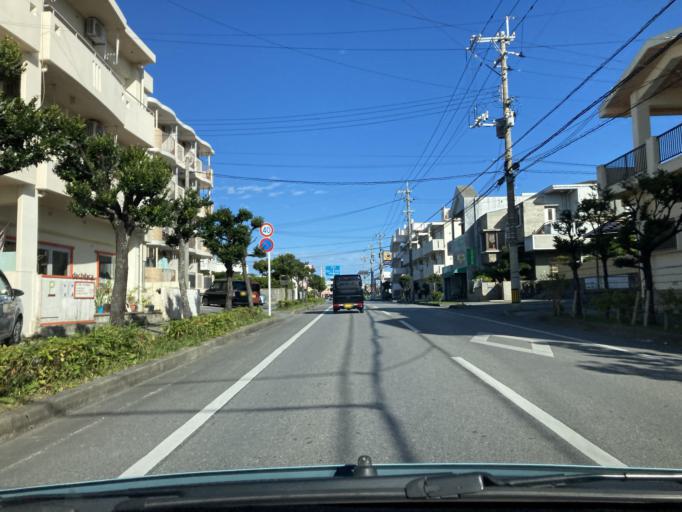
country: JP
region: Okinawa
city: Okinawa
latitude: 26.3685
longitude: 127.7471
